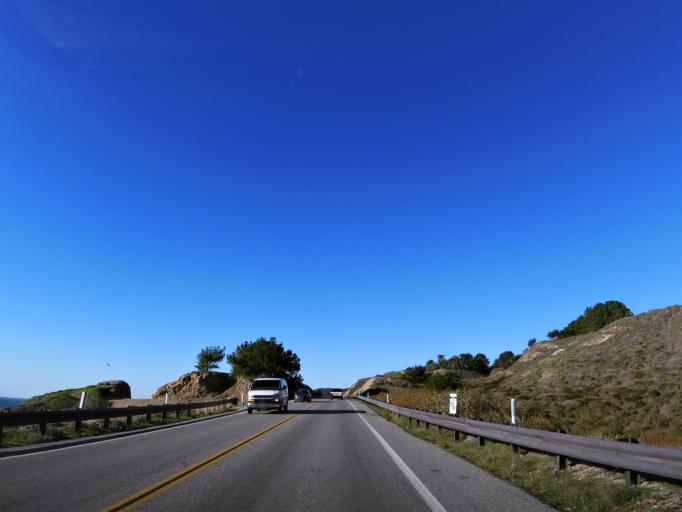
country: US
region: California
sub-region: Santa Cruz County
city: Bonny Doon
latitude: 37.0669
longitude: -122.2553
